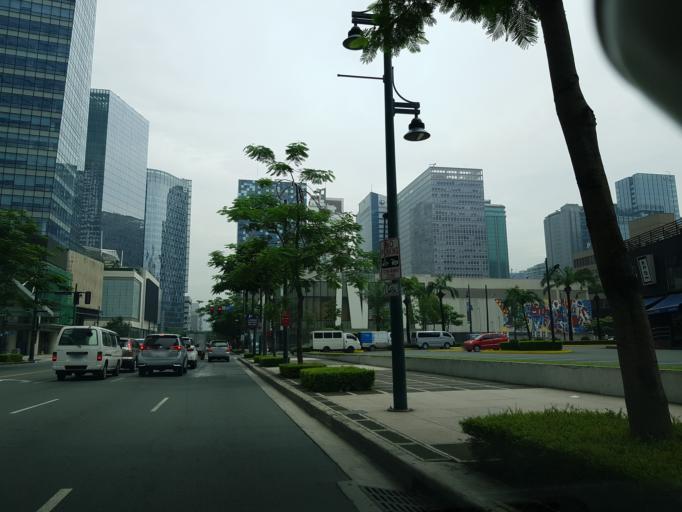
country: PH
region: Metro Manila
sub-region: Makati City
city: Makati City
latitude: 14.5500
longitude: 121.0472
